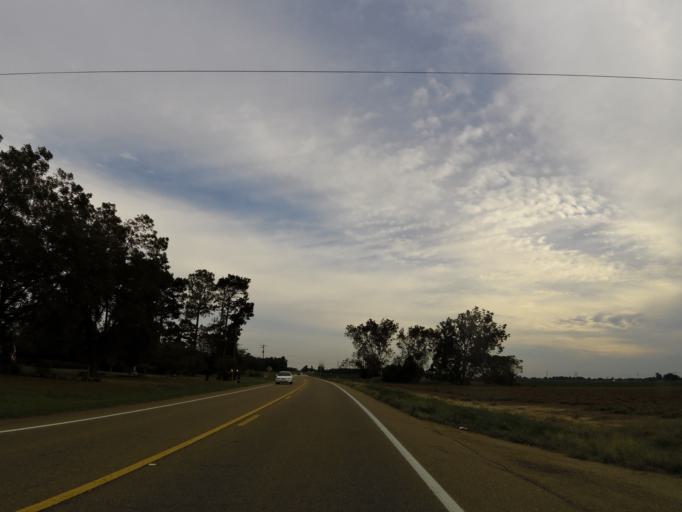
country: US
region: Alabama
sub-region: Monroe County
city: Frisco City
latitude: 31.4114
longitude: -87.4290
